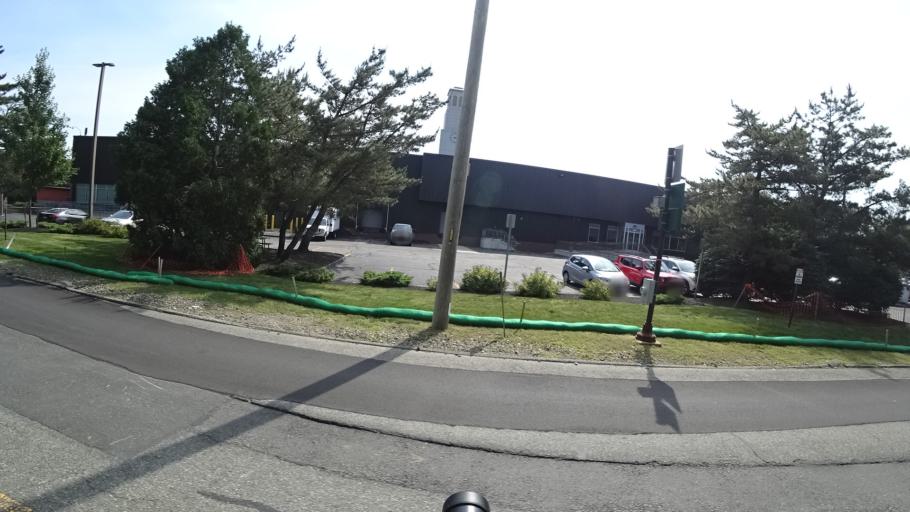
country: US
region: Massachusetts
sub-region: Norfolk County
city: Dedham
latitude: 42.2315
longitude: -71.1714
